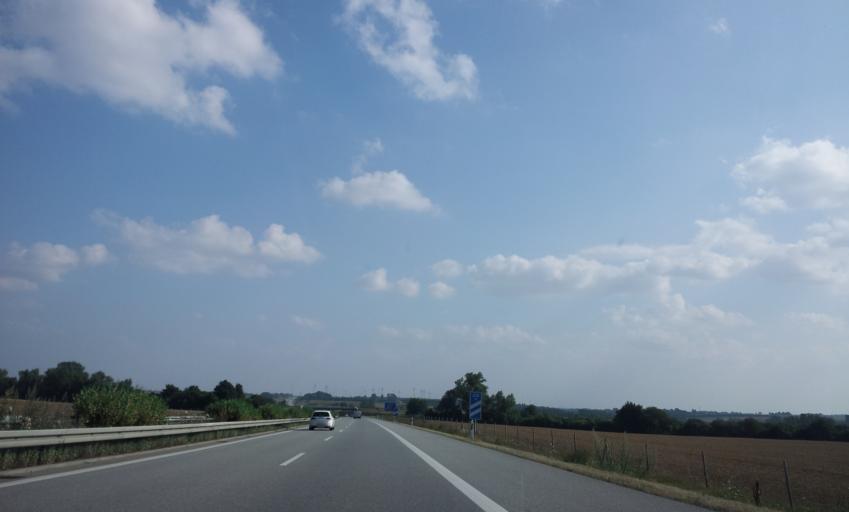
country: DE
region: Mecklenburg-Vorpommern
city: Burow
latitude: 53.7994
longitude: 13.3218
